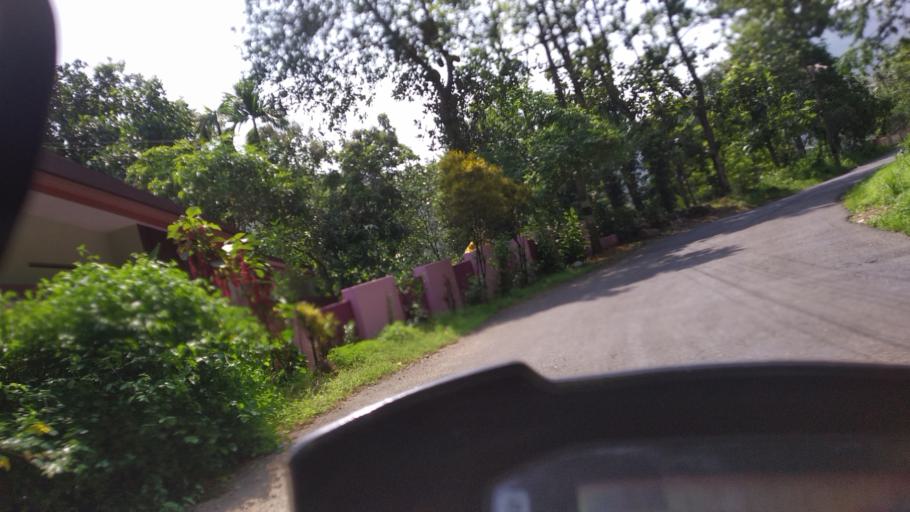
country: IN
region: Kerala
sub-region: Kottayam
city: Erattupetta
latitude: 9.6908
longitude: 76.8521
